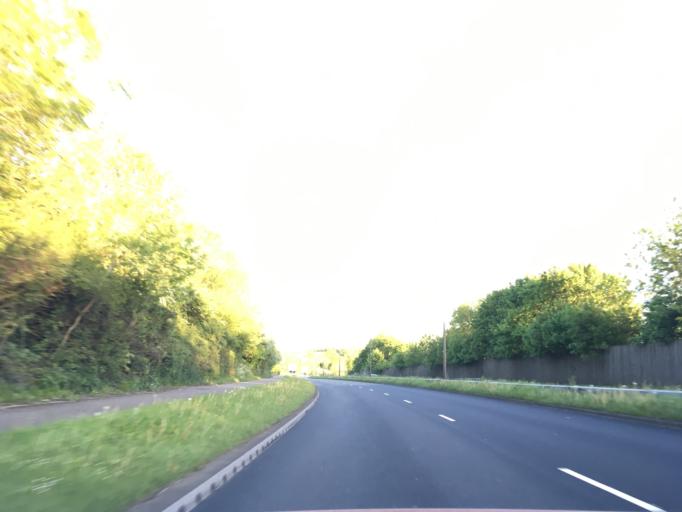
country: GB
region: Wales
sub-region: Newport
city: Llanwern
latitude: 51.5961
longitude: -2.9256
